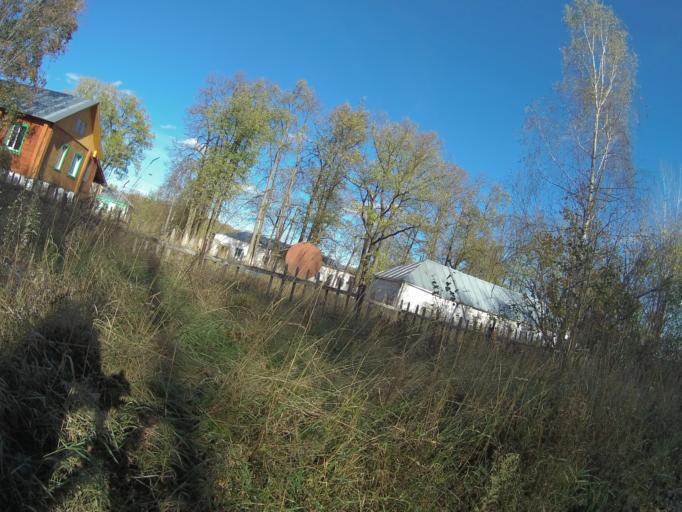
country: RU
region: Vladimir
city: Golovino
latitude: 55.9977
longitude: 40.5014
